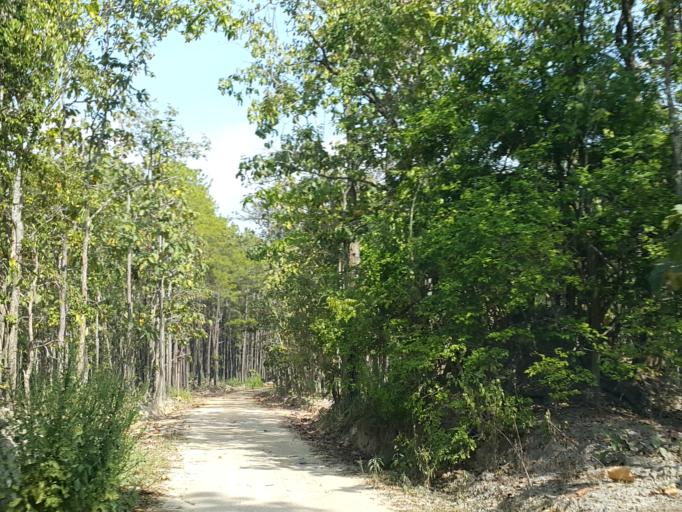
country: TH
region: Chiang Mai
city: Hot
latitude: 18.1386
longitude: 98.4269
